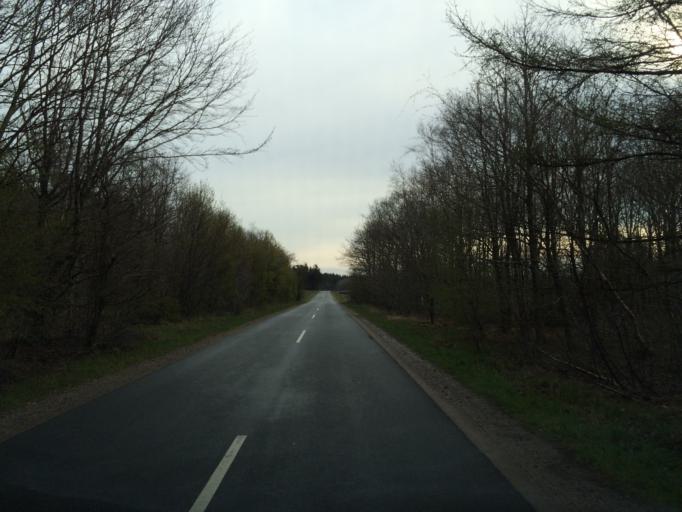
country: DK
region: Central Jutland
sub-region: Holstebro Kommune
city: Ulfborg
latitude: 56.2031
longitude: 8.4580
